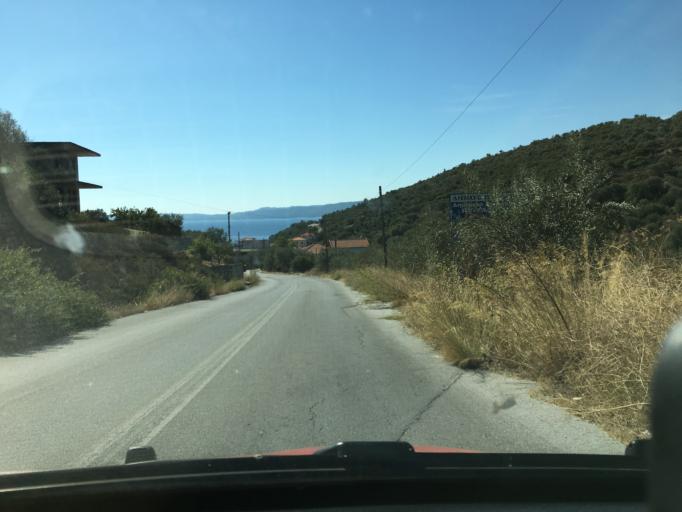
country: GR
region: Central Macedonia
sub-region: Nomos Chalkidikis
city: Agios Nikolaos
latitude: 40.3394
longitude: 23.7204
